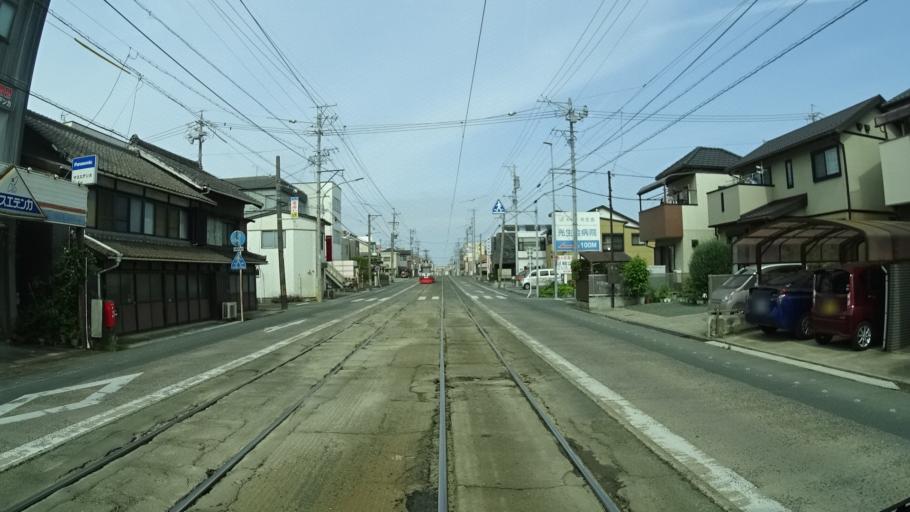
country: JP
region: Aichi
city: Toyohashi
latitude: 34.7652
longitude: 137.4153
